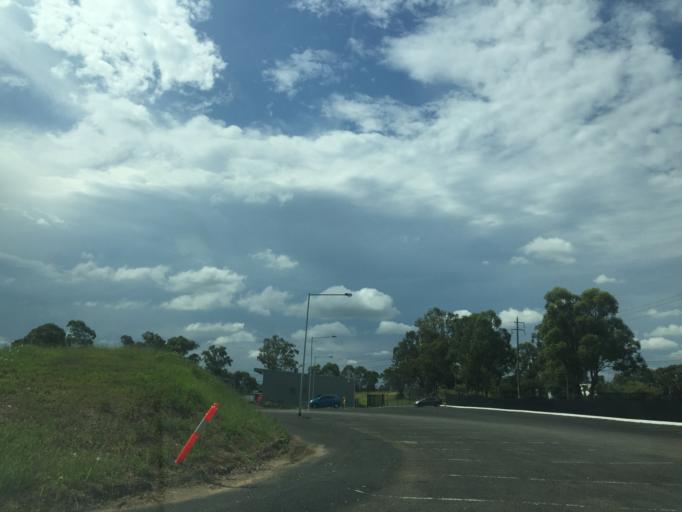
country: AU
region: New South Wales
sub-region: Holroyd
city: Girraween
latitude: -33.8076
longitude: 150.9134
